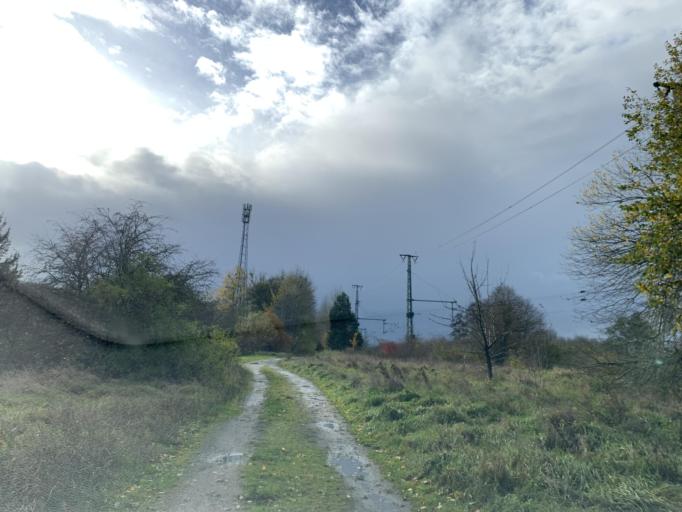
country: DE
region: Mecklenburg-Vorpommern
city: Blankensee
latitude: 53.4046
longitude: 13.2604
